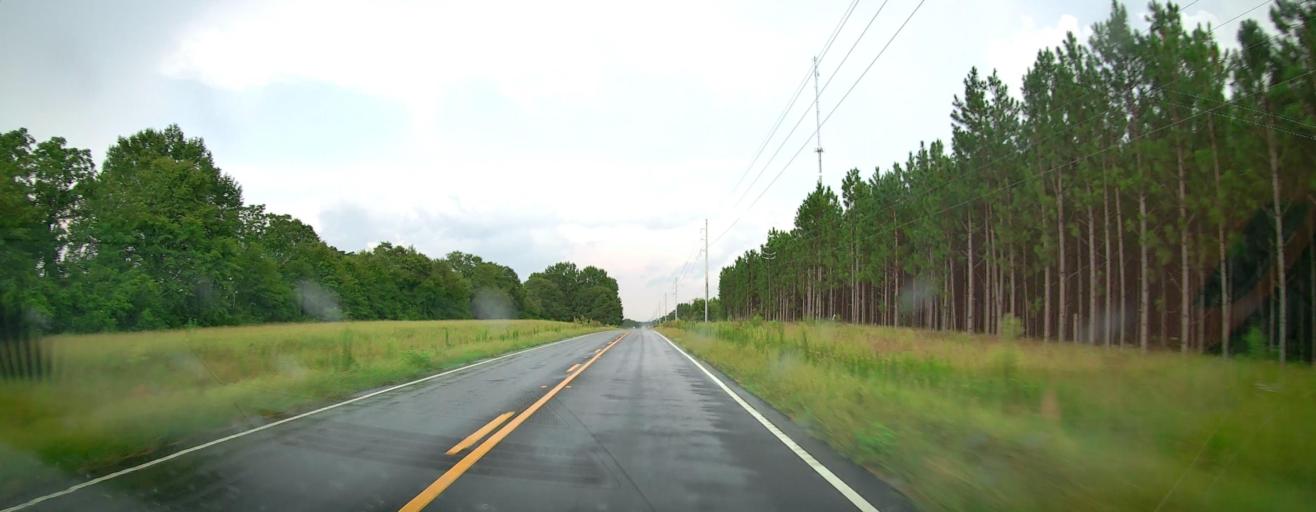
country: US
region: Georgia
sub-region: Dodge County
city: Chester
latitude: 32.5719
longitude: -83.1929
